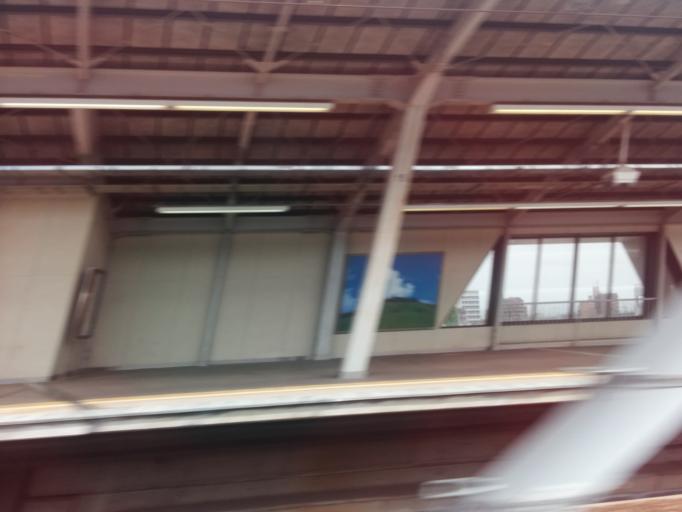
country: JP
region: Aichi
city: Anjo
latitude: 34.9695
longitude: 137.0601
